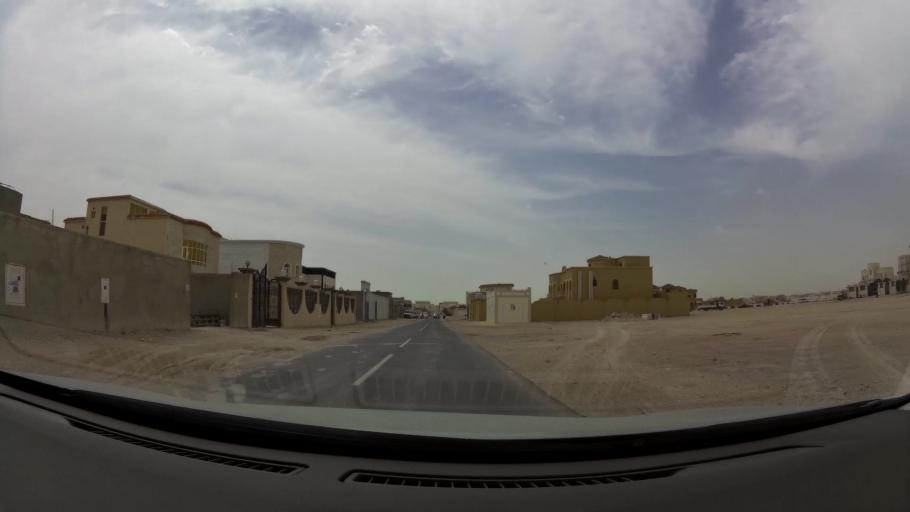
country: QA
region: Baladiyat ar Rayyan
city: Ar Rayyan
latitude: 25.2108
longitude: 51.4636
